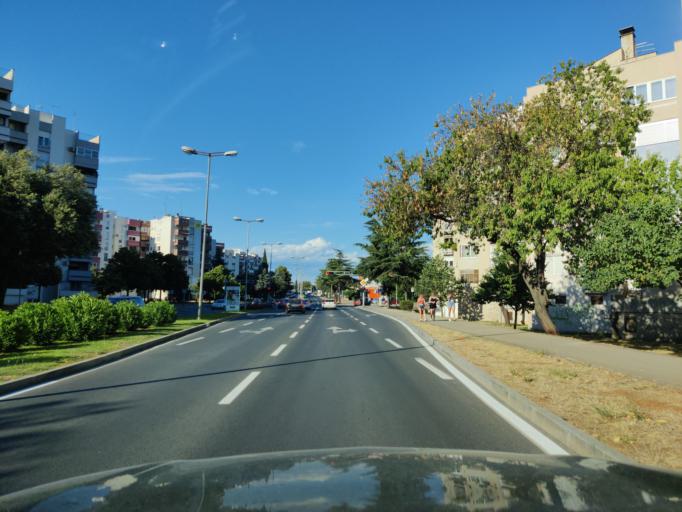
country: HR
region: Zadarska
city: Zadar
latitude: 44.1083
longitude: 15.2444
